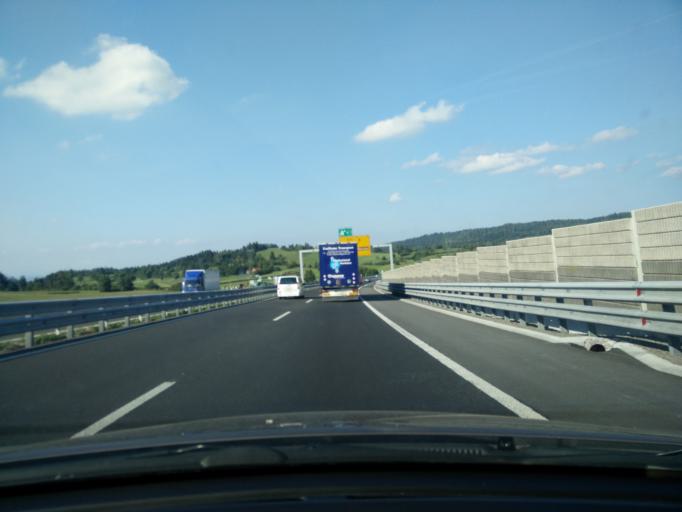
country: SI
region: Cerknica
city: Rakek
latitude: 45.8207
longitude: 14.2856
